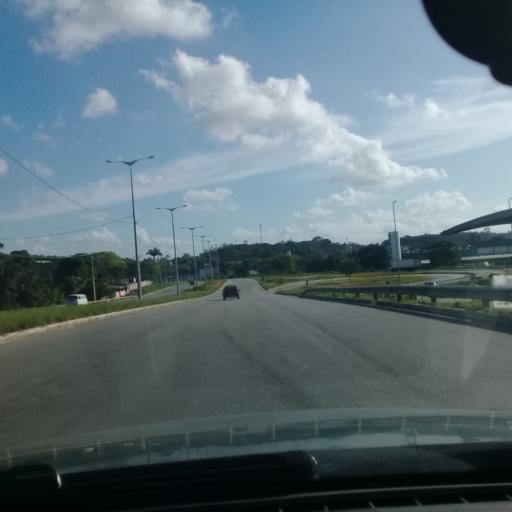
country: BR
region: Pernambuco
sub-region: Abreu E Lima
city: Abreu e Lima
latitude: -7.9217
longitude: -34.8945
